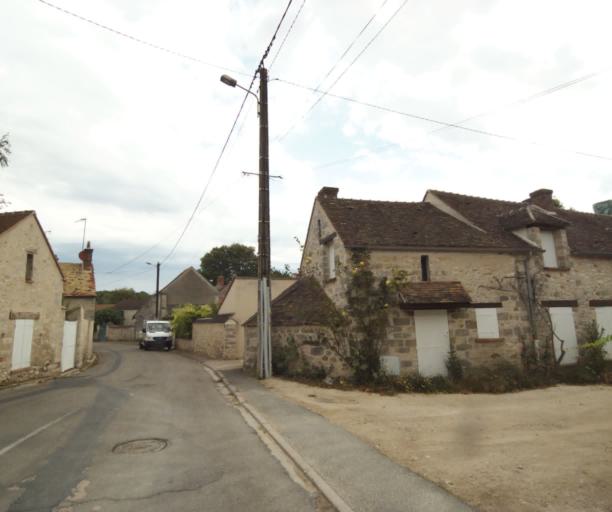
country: FR
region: Ile-de-France
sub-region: Departement de Seine-et-Marne
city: Cely
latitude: 48.4578
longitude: 2.5375
